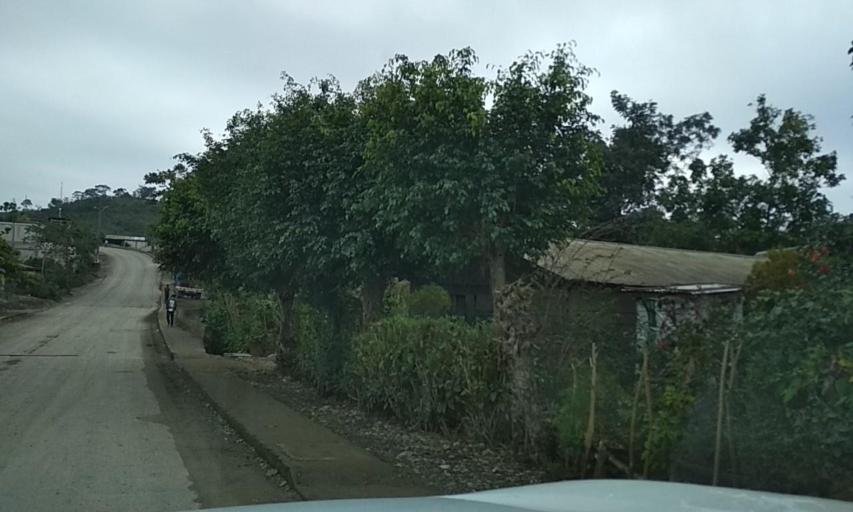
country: MX
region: Veracruz
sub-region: Coatzintla
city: Manuel Maria Contreras
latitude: 20.3601
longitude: -97.5122
